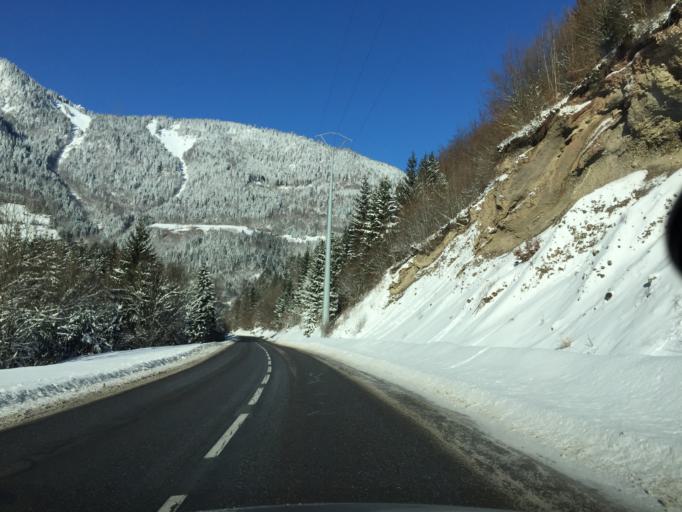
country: FR
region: Rhone-Alpes
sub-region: Departement de la Haute-Savoie
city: Abondance
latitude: 46.2944
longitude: 6.6821
